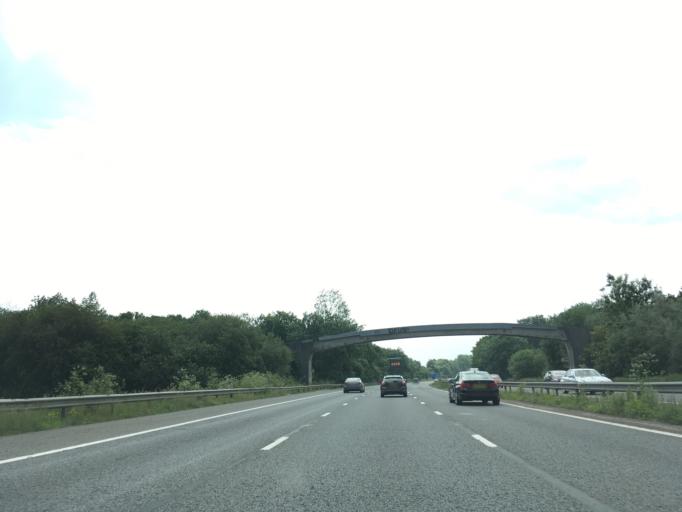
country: GB
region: England
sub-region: West Berkshire
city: Theale
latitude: 51.4530
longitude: -1.0798
